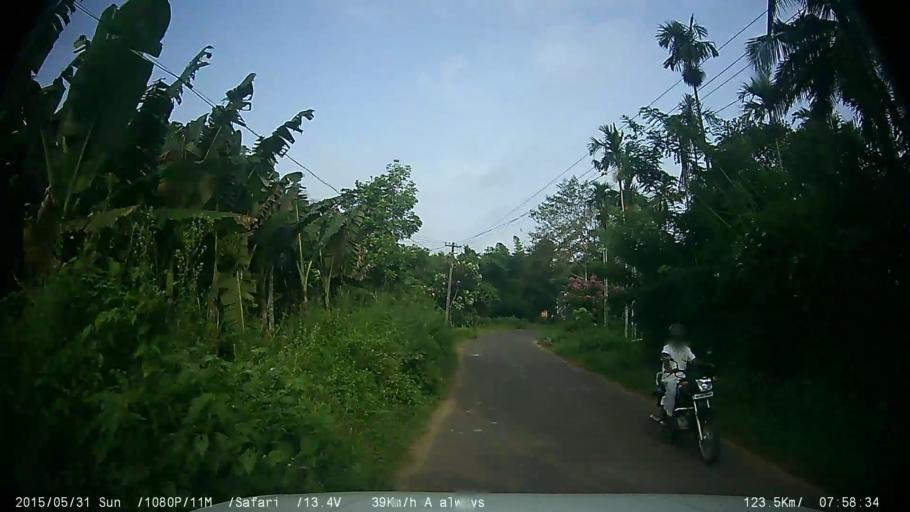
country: IN
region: Kerala
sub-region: Wayanad
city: Kalpetta
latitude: 11.6346
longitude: 76.0614
